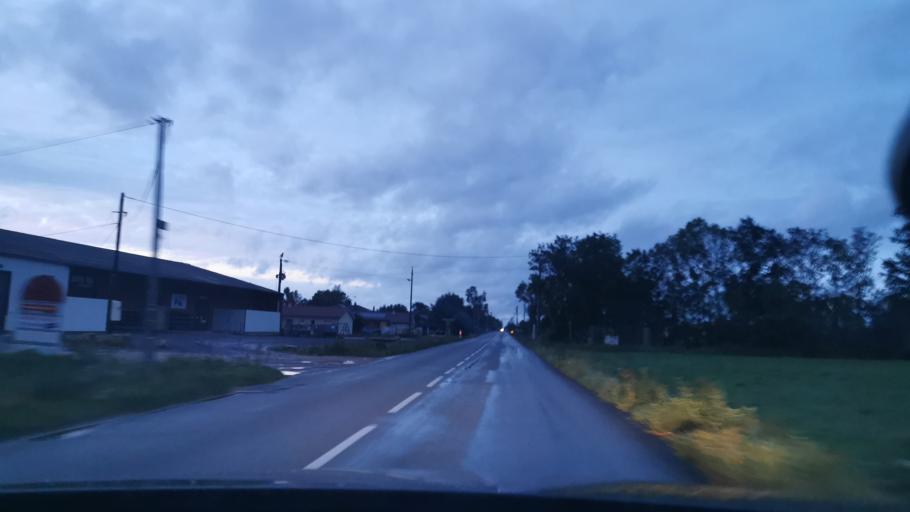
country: FR
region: Rhone-Alpes
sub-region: Departement de l'Ain
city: Bage-la-Ville
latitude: 46.3242
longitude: 4.9348
